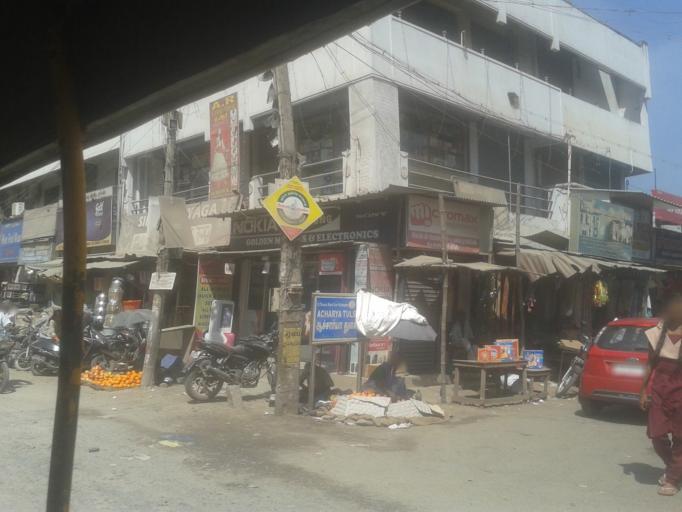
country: IN
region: Tamil Nadu
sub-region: Kancheepuram
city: Pallavaram
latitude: 12.9690
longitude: 80.1471
